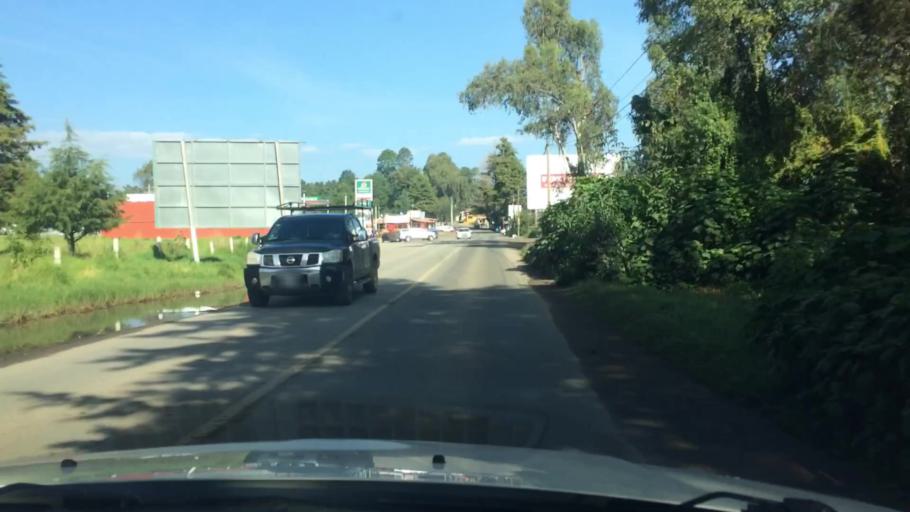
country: MX
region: Mexico
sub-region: Valle de Bravo
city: Cuadrilla de Dolores
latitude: 19.1466
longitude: -100.0693
